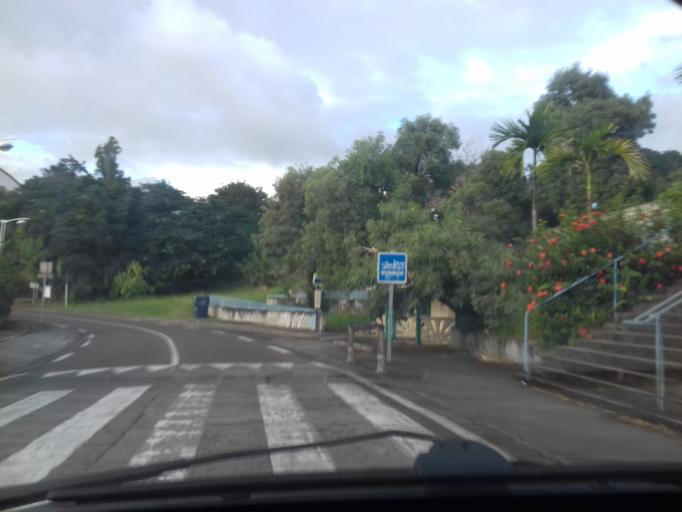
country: MQ
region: Martinique
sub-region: Martinique
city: Fort-de-France
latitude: 14.6195
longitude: -61.0952
